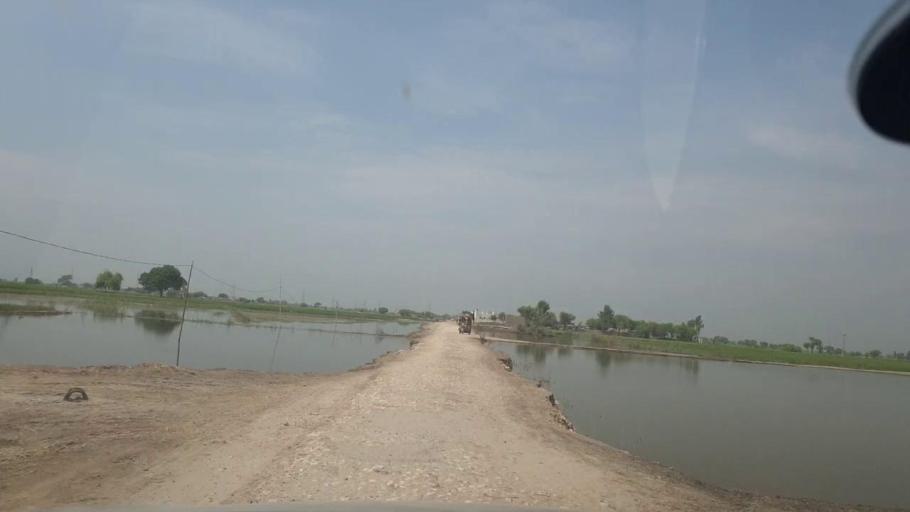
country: PK
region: Sindh
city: Thul
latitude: 28.1719
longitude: 68.6300
